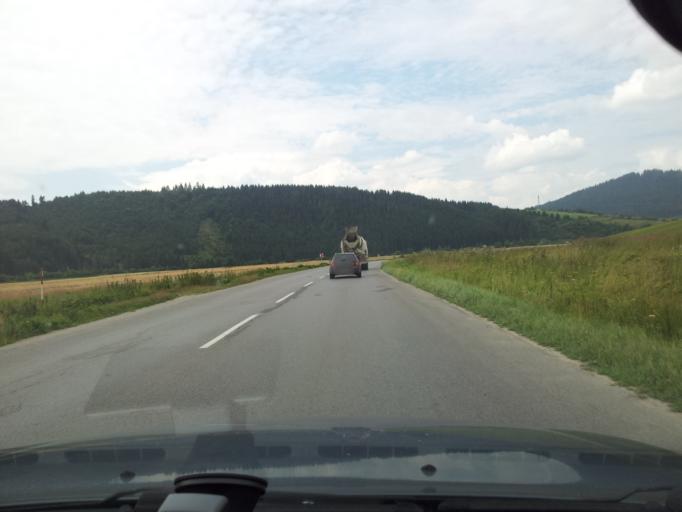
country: SK
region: Zilinsky
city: Namestovo
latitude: 49.3743
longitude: 19.3924
